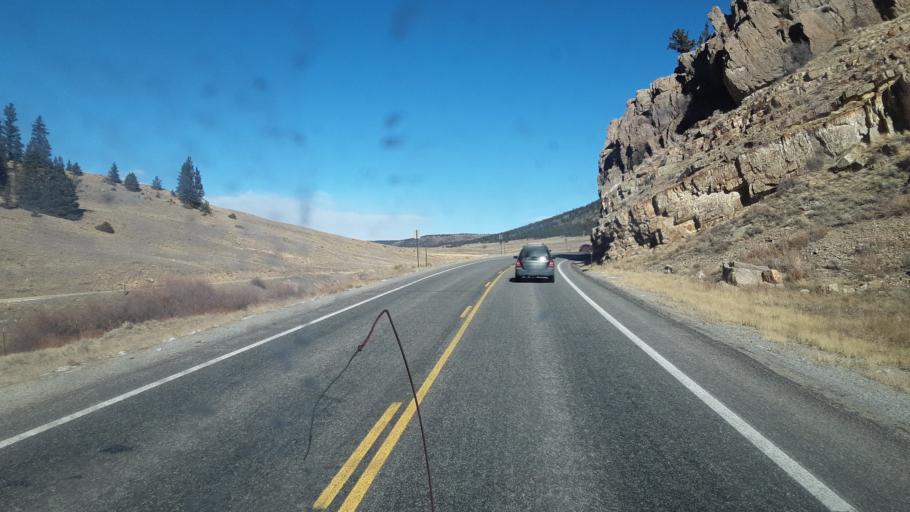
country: US
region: Colorado
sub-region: Chaffee County
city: Buena Vista
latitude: 38.8596
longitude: -105.9863
